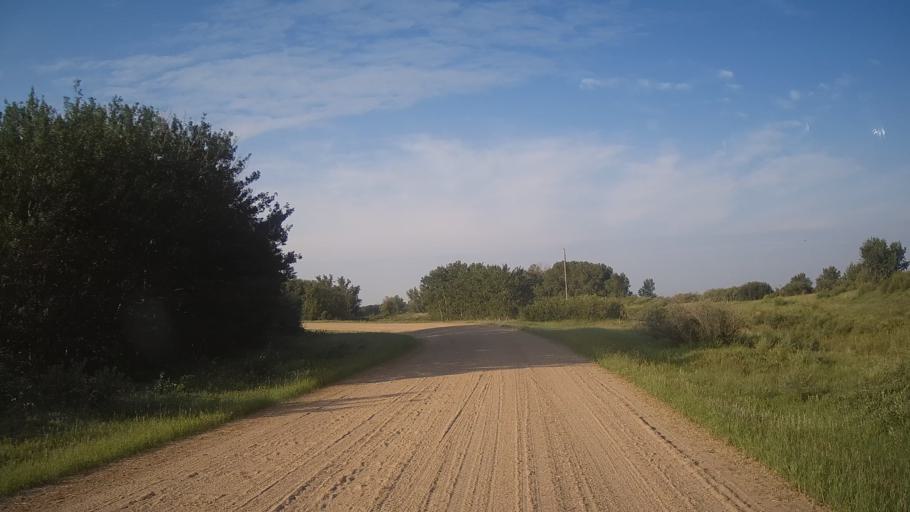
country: CA
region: Saskatchewan
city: Saskatoon
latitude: 51.8256
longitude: -106.5423
